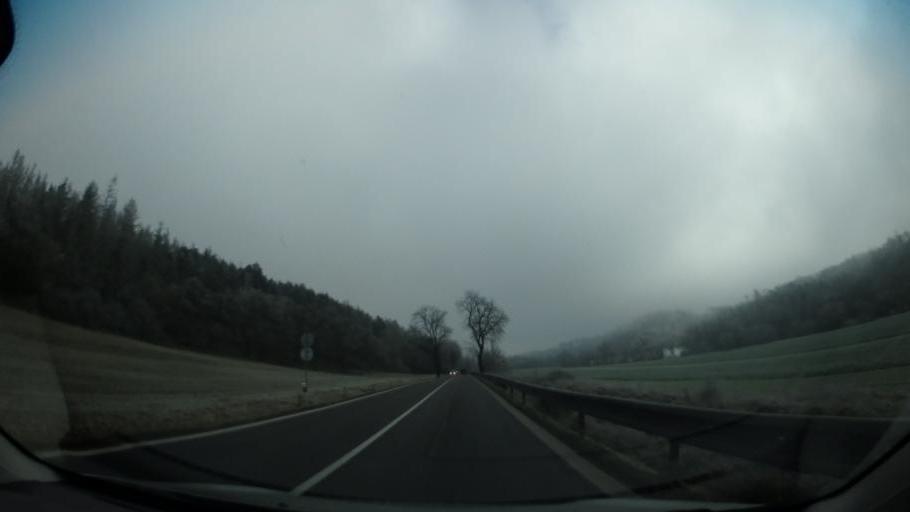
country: CZ
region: Vysocina
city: Vladislav
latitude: 49.2152
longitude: 15.9423
